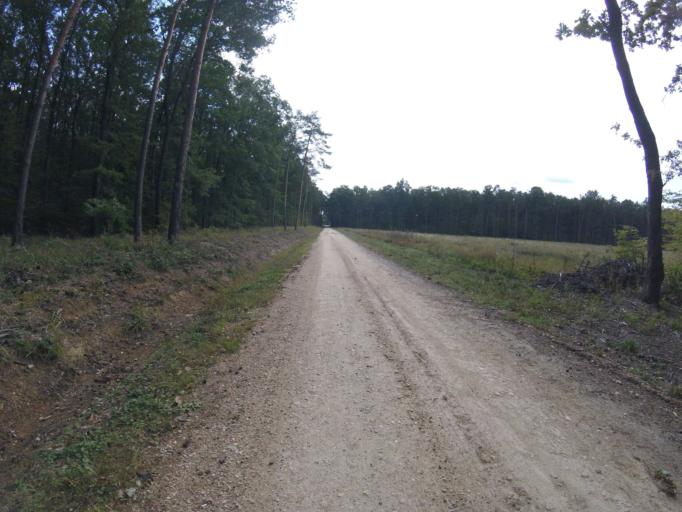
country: HU
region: Vas
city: Koszeg
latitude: 47.3771
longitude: 16.6006
